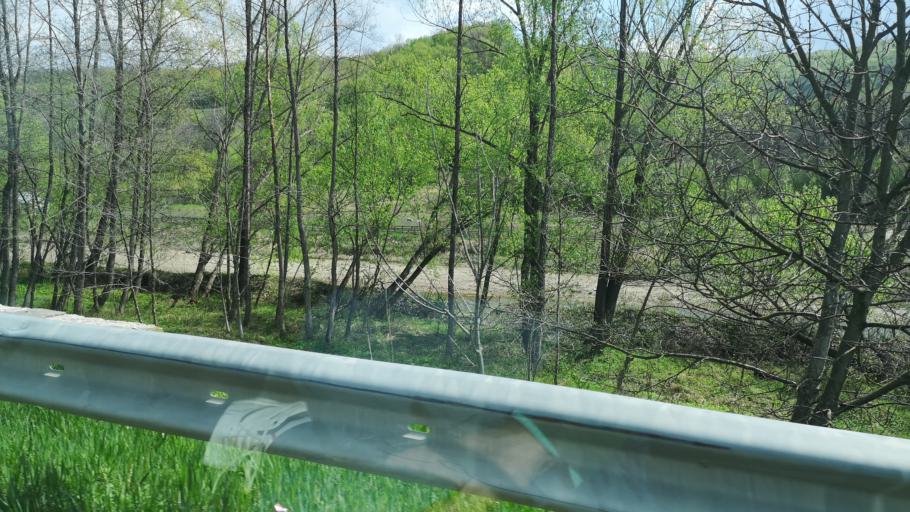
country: RO
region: Prahova
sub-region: Comuna Soimari
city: Soimari
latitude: 45.1645
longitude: 26.2098
